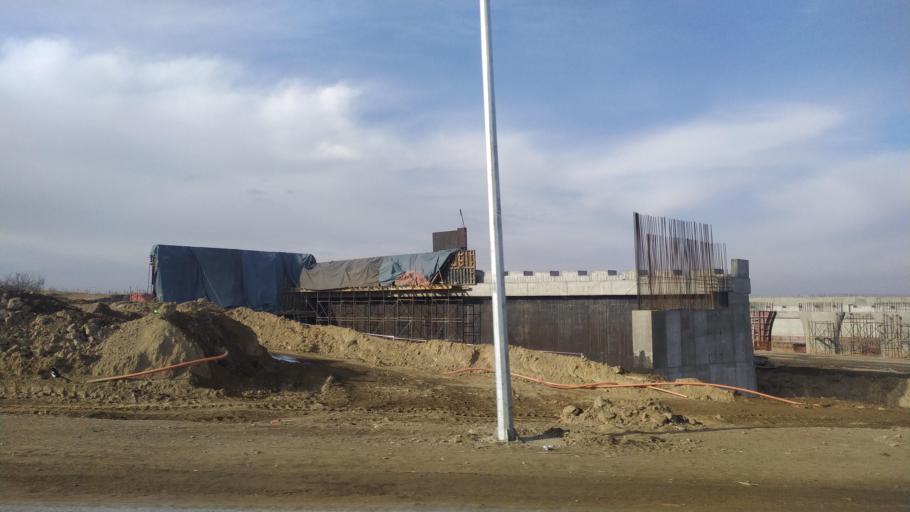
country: KZ
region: Almaty Oblysy
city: Burunday
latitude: 43.2246
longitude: 76.7295
